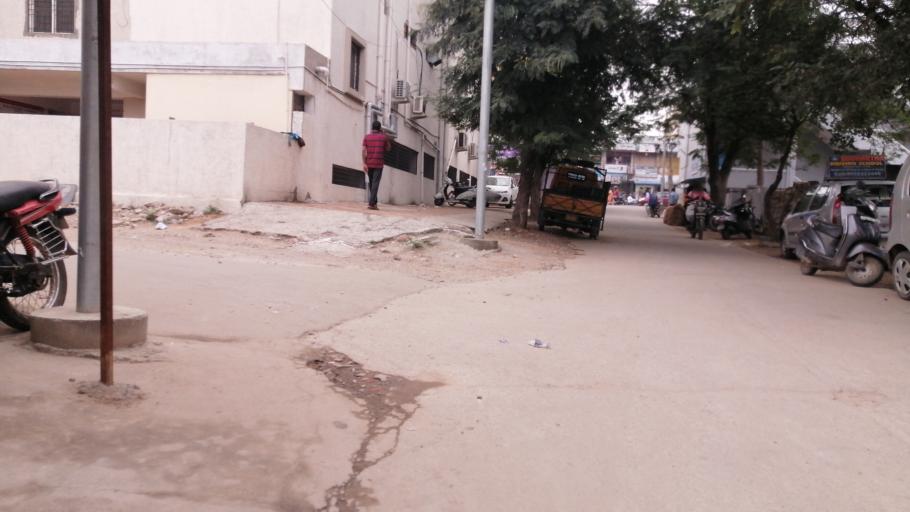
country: IN
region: Telangana
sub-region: Rangareddi
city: Secunderabad
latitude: 17.4808
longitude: 78.5806
